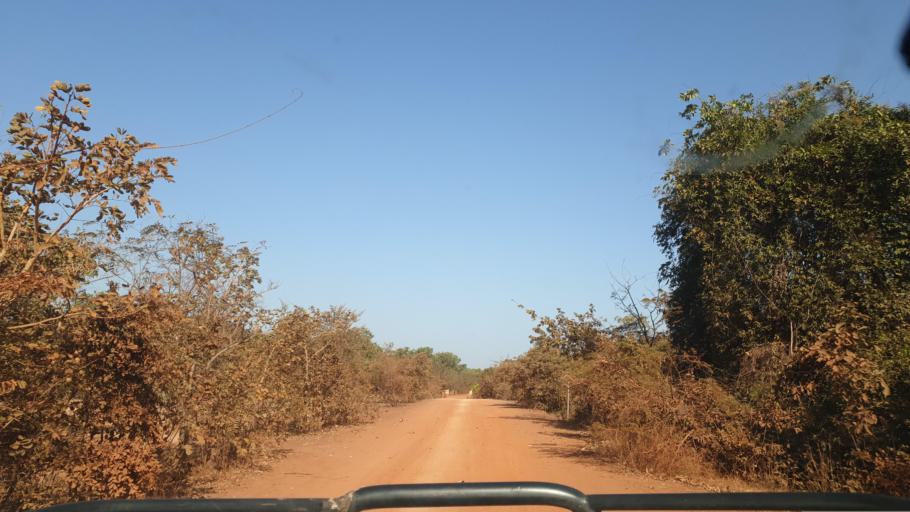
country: ML
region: Sikasso
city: Bougouni
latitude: 11.7772
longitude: -6.9068
